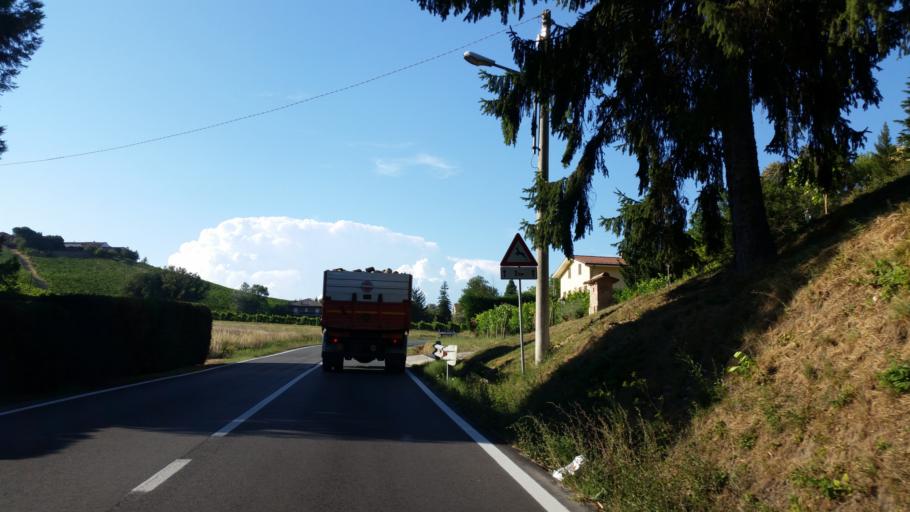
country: IT
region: Piedmont
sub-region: Provincia di Asti
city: Castel Boglione
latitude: 44.7244
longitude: 8.3808
